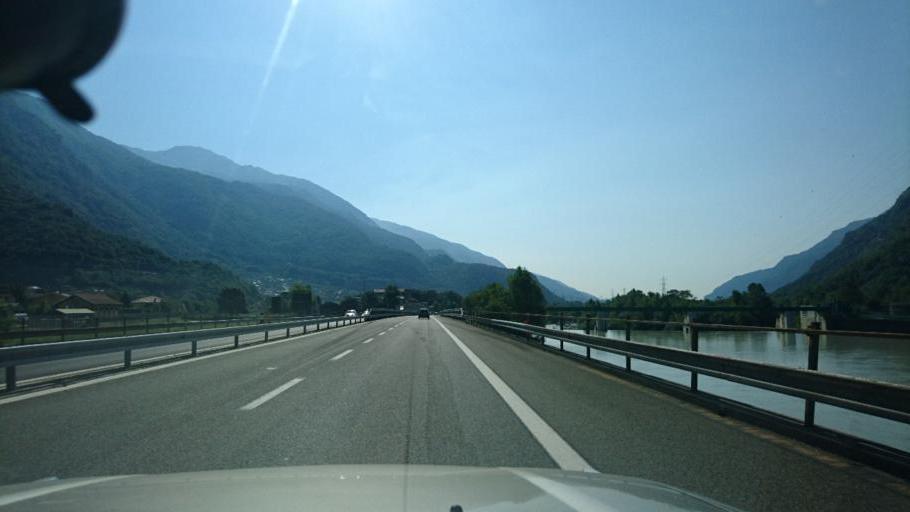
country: IT
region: Aosta Valley
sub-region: Valle d'Aosta
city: Pont-Saint-Martin
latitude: 45.5901
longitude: 7.7928
